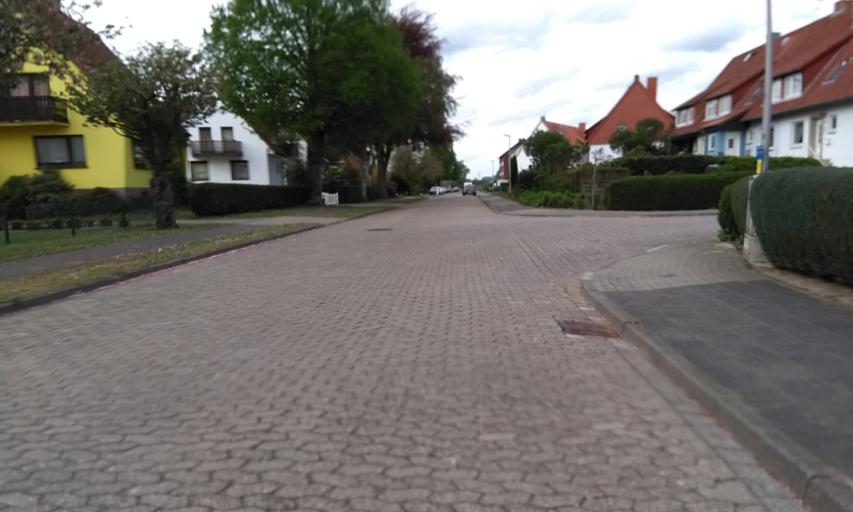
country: DE
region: Lower Saxony
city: Buxtehude
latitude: 53.4742
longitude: 9.6804
